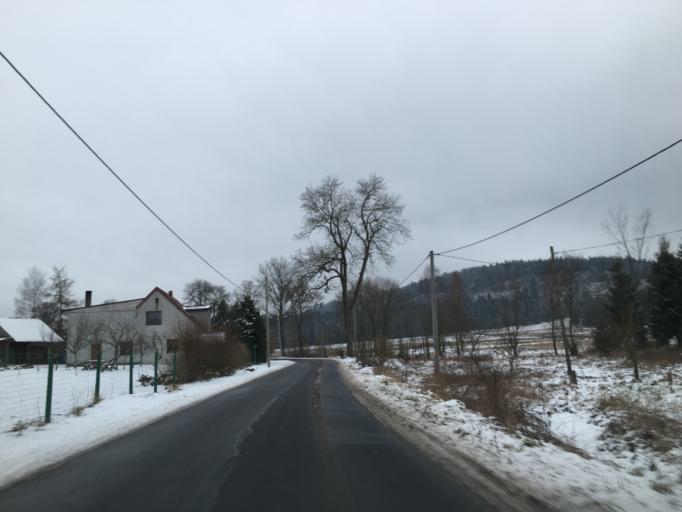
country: PL
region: Lower Silesian Voivodeship
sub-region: Powiat walbrzyski
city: Mieroszow
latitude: 50.6907
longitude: 16.1515
